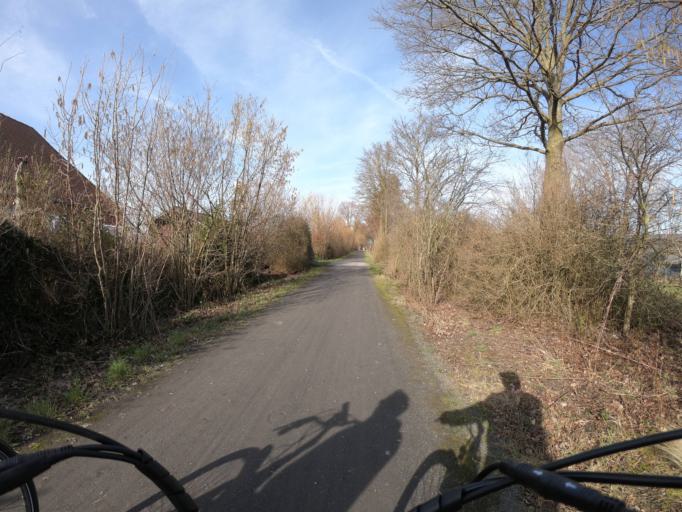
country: BE
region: Flanders
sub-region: Provincie West-Vlaanderen
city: Menen
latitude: 50.8244
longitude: 3.1247
